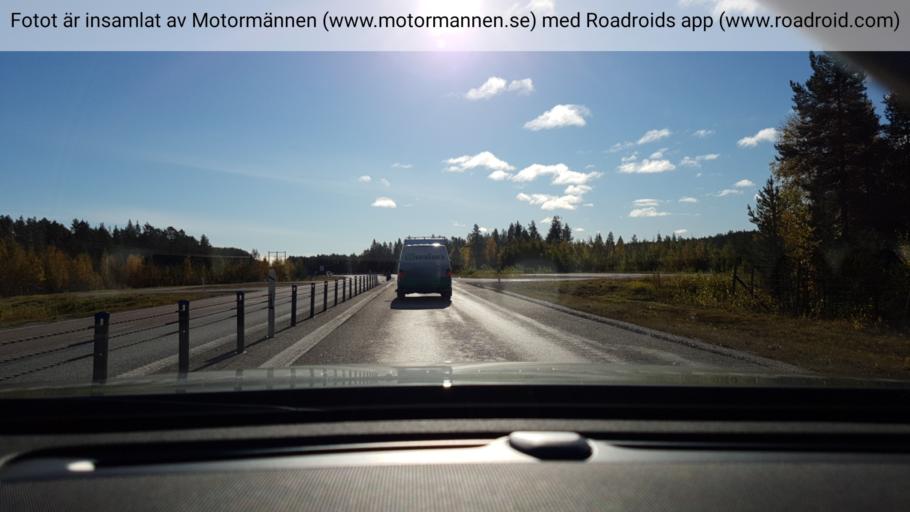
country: SE
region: Vaesterbotten
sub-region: Skelleftea Kommun
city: Soedra Bergsbyn
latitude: 64.6658
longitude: 21.0988
